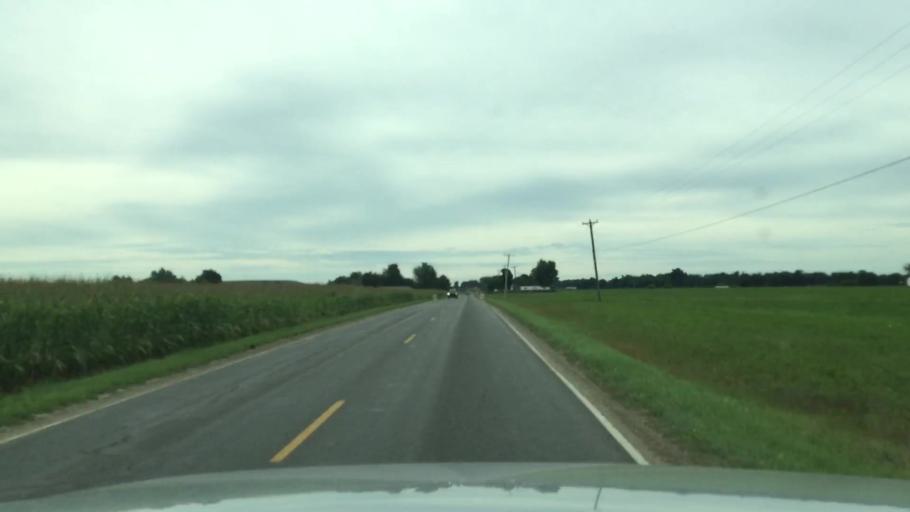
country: US
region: Michigan
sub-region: Shiawassee County
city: Durand
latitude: 43.0056
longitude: -83.9870
